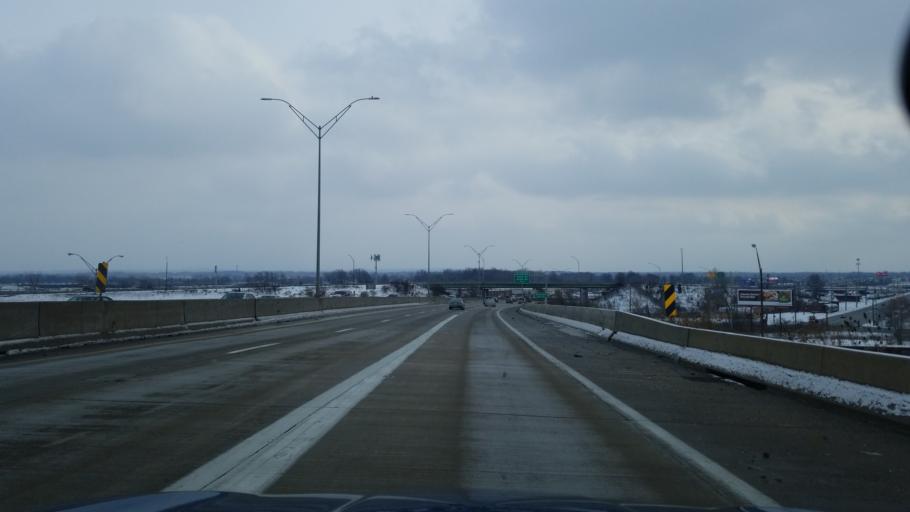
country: US
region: Ohio
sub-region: Cuyahoga County
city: Brook Park
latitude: 41.4211
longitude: -81.8195
